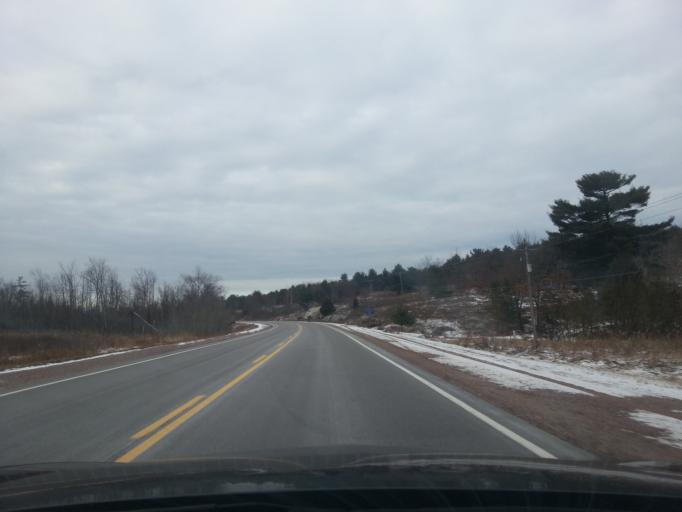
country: CA
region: Ontario
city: Greater Napanee
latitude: 44.6580
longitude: -77.0996
